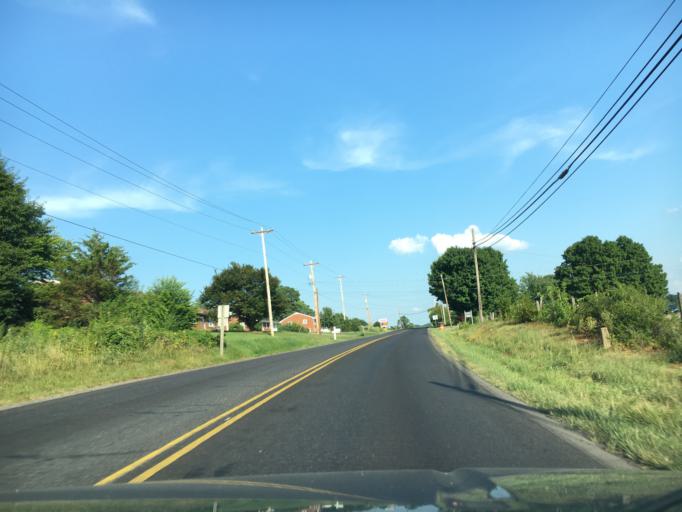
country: US
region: Virginia
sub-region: Franklin County
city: Henry Fork
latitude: 37.0197
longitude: -79.8111
